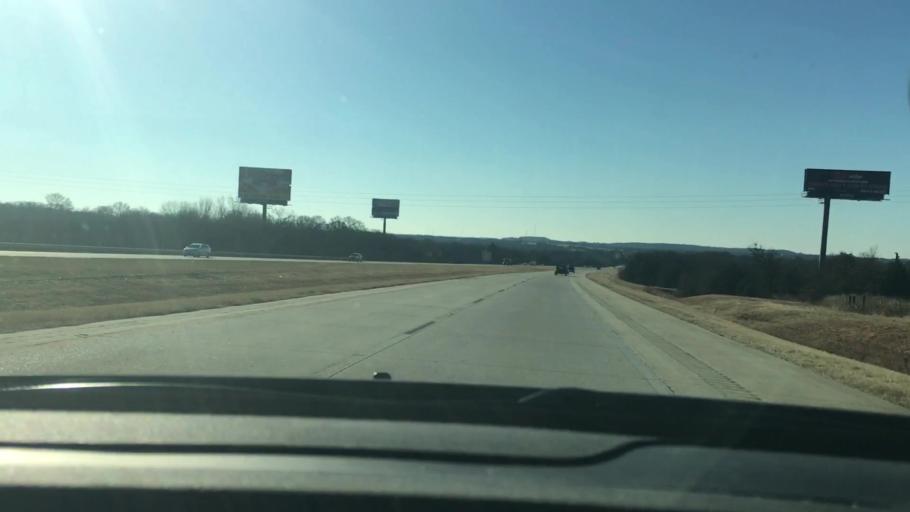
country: US
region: Oklahoma
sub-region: Carter County
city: Ardmore
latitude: 34.0566
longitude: -97.1490
